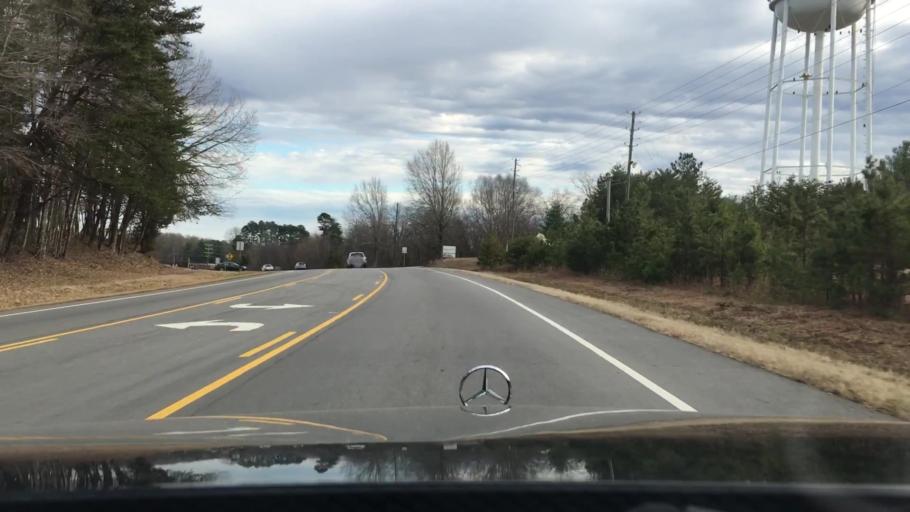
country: US
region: North Carolina
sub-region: Caswell County
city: Yanceyville
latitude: 36.4089
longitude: -79.3405
